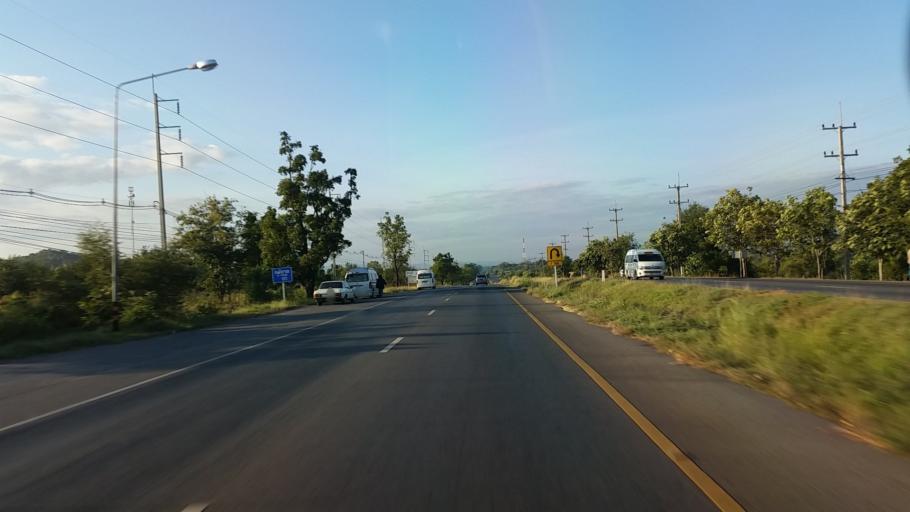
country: TH
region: Lop Buri
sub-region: Amphoe Tha Luang
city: Tha Luang
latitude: 15.1332
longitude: 101.0412
